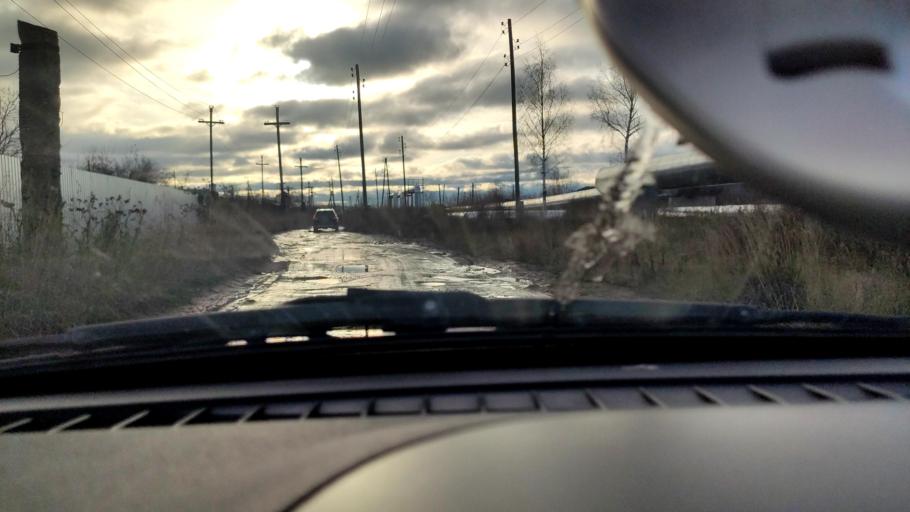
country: RU
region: Perm
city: Kondratovo
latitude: 57.9576
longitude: 56.1441
